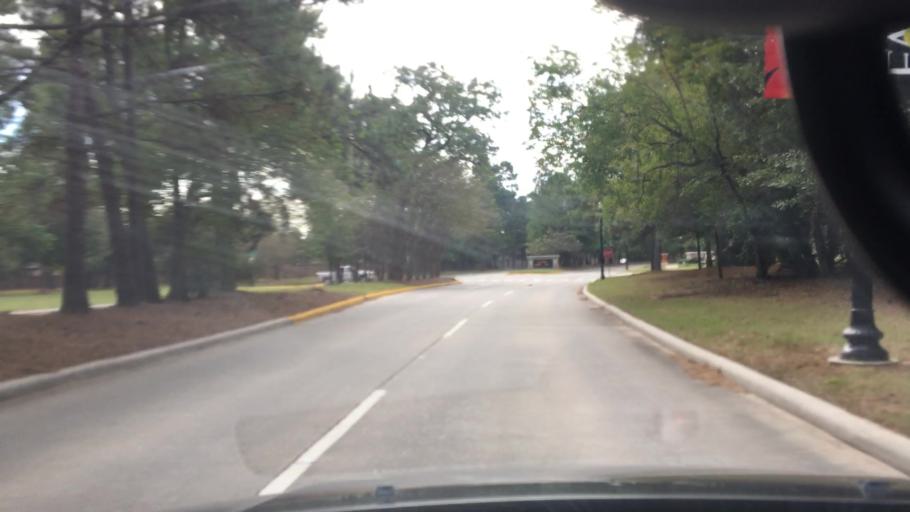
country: US
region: Texas
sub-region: Harris County
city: Humble
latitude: 29.9339
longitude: -95.2688
